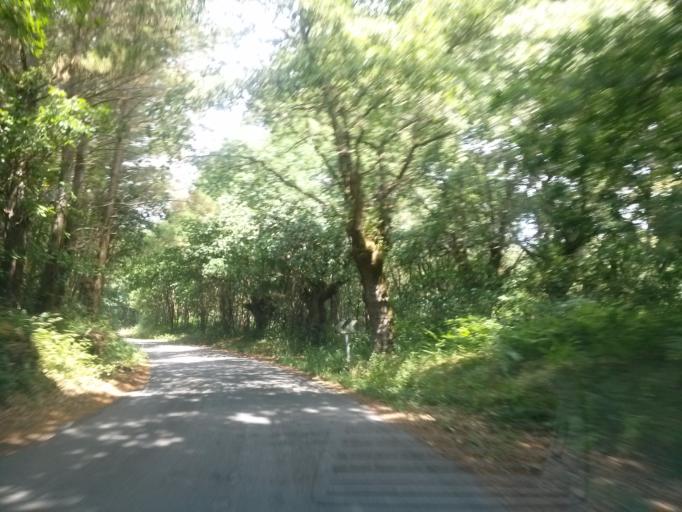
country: ES
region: Galicia
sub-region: Provincia de Lugo
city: Outeiro de Rei
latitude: 43.0429
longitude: -7.6144
